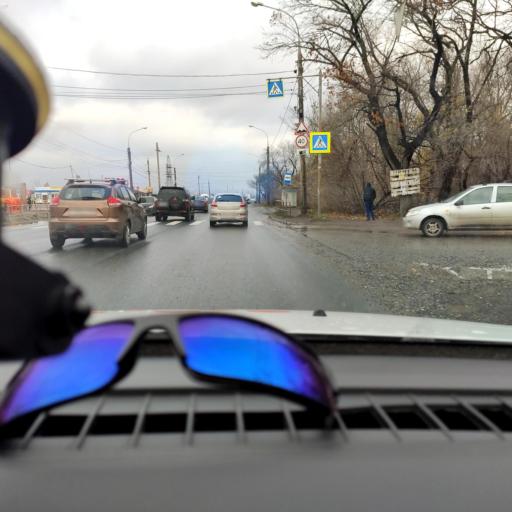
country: RU
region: Samara
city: Samara
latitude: 53.1310
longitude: 50.1725
